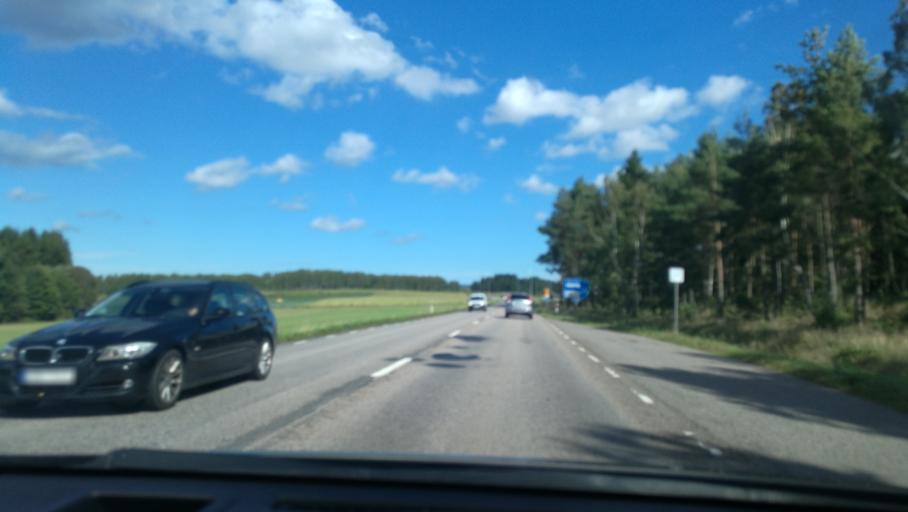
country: SE
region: Vaestra Goetaland
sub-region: Gotene Kommun
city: Kallby
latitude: 58.4972
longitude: 13.2995
